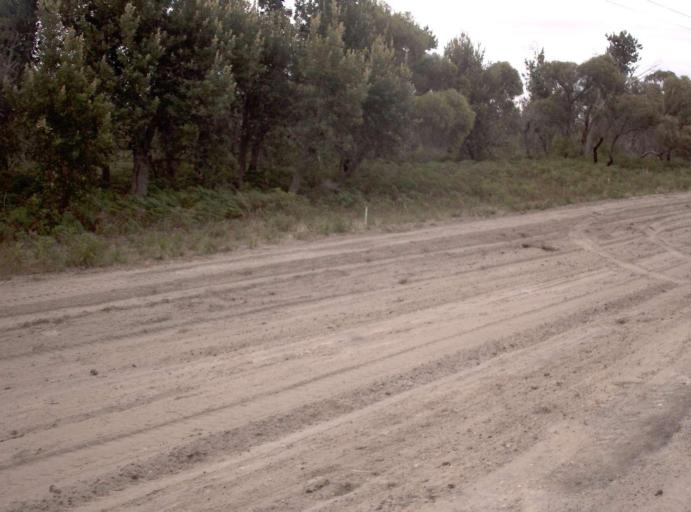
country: AU
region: Victoria
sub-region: East Gippsland
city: Bairnsdale
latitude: -38.0778
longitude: 147.5377
